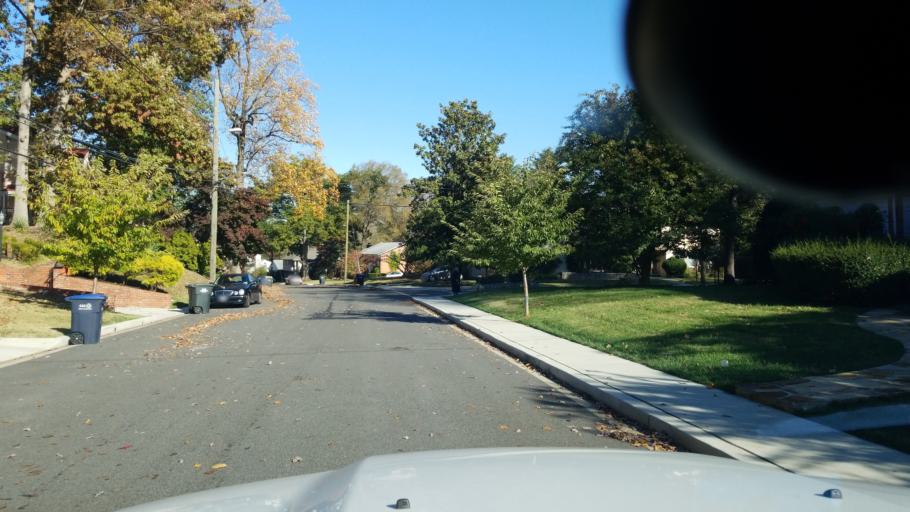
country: US
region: Maryland
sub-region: Montgomery County
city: Chevy Chase
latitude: 38.9814
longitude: -77.0559
